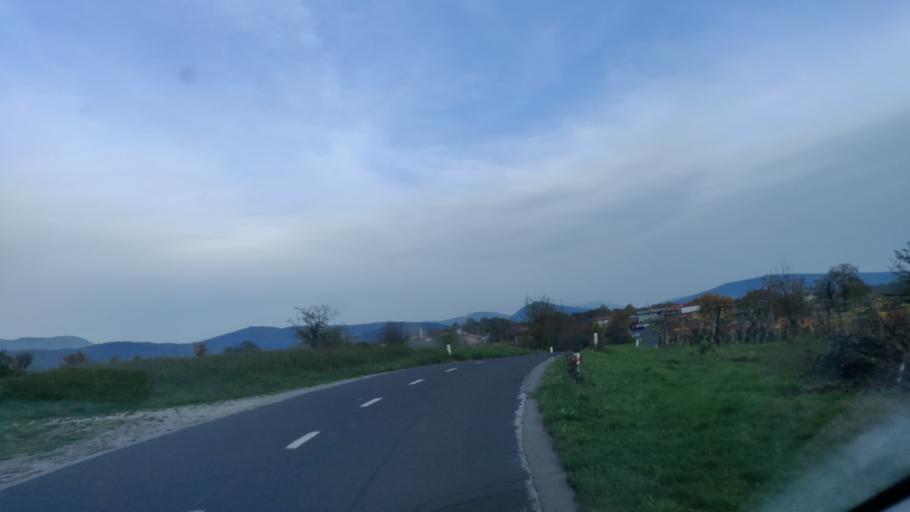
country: SI
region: Sezana
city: Sezana
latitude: 45.7632
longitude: 13.9018
